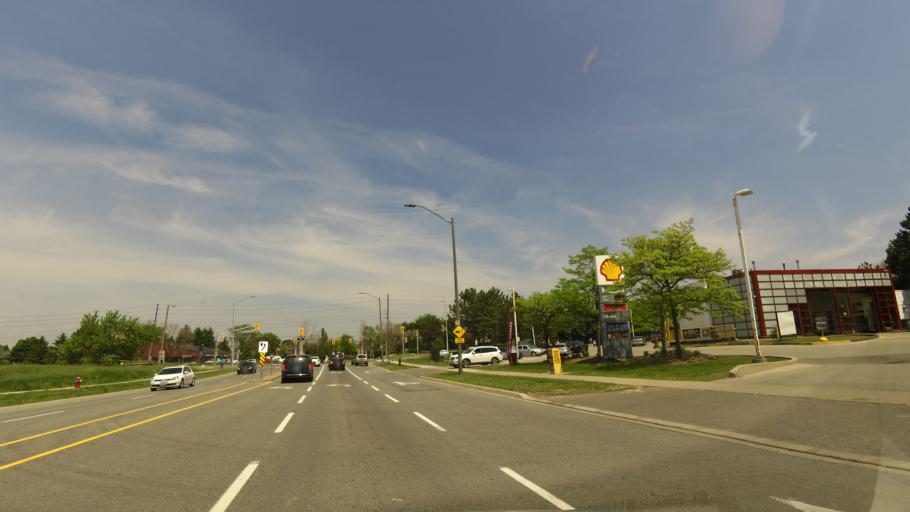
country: CA
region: Ontario
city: Mississauga
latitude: 43.5390
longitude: -79.7059
